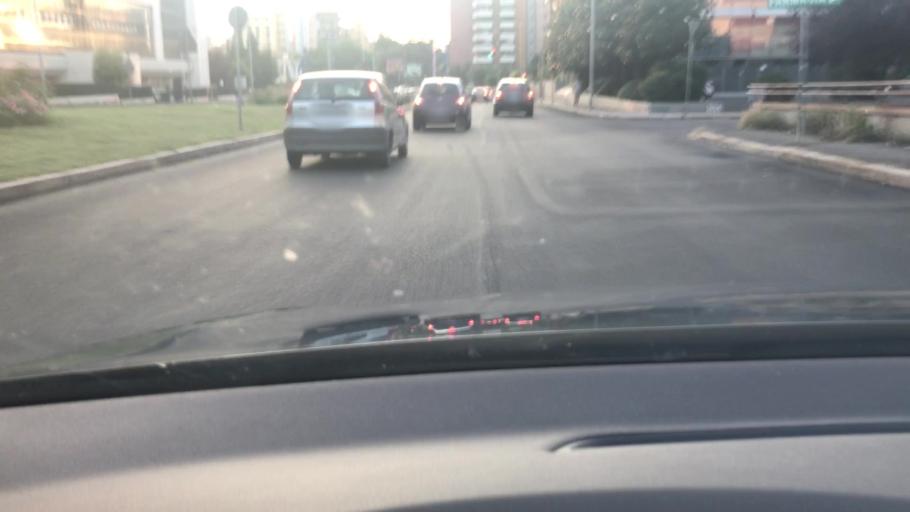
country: IT
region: Latium
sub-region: Citta metropolitana di Roma Capitale
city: Rome
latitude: 41.9300
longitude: 12.5623
